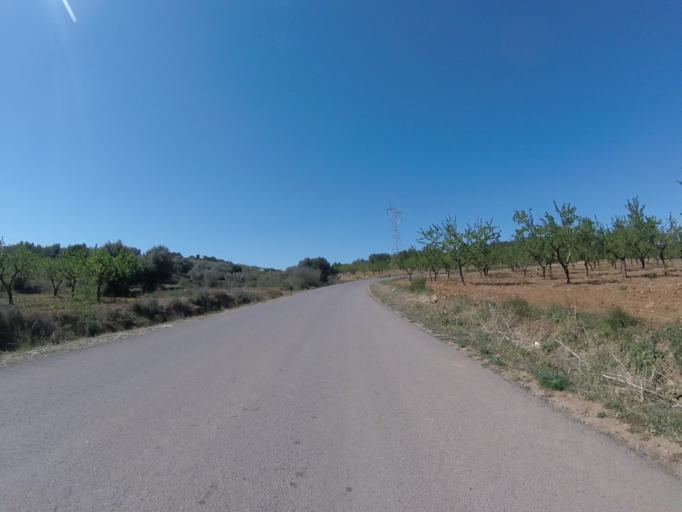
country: ES
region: Valencia
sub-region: Provincia de Castello
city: Cuevas de Vinroma
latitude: 40.3790
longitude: 0.1409
